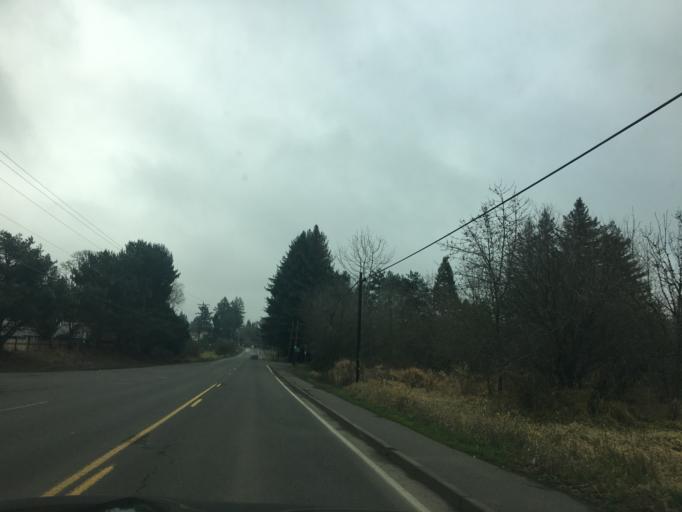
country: US
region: Oregon
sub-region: Washington County
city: Aloha
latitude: 45.4707
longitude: -122.8793
